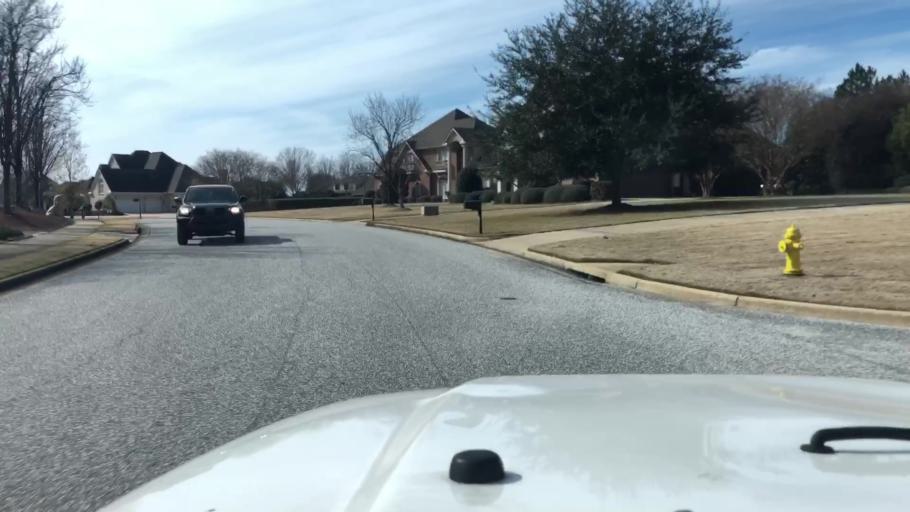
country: US
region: Alabama
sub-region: Montgomery County
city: Pike Road
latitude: 32.3560
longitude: -86.1541
